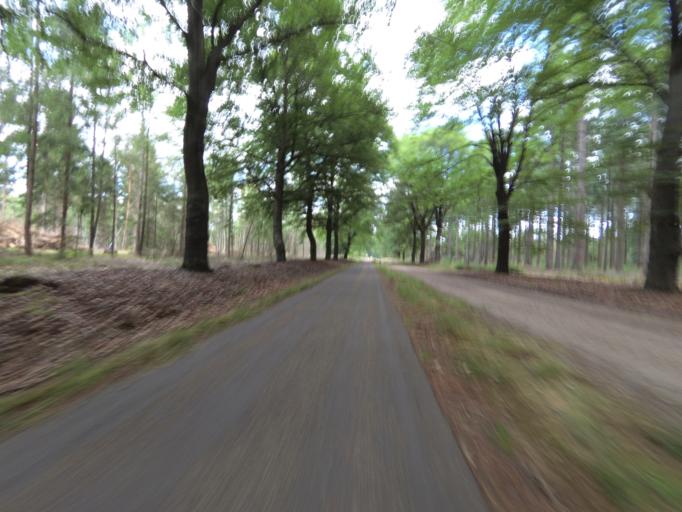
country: NL
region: Overijssel
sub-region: Gemeente Hof van Twente
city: Markelo
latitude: 52.3286
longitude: 6.4487
